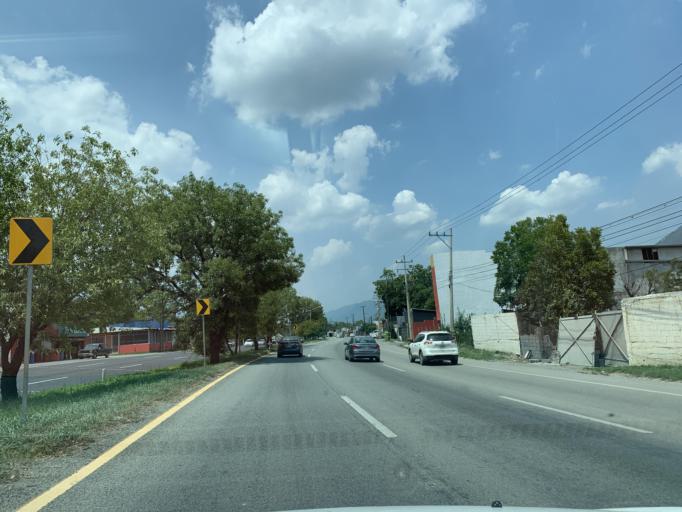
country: MX
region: Nuevo Leon
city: Santiago
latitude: 25.4151
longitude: -100.1414
